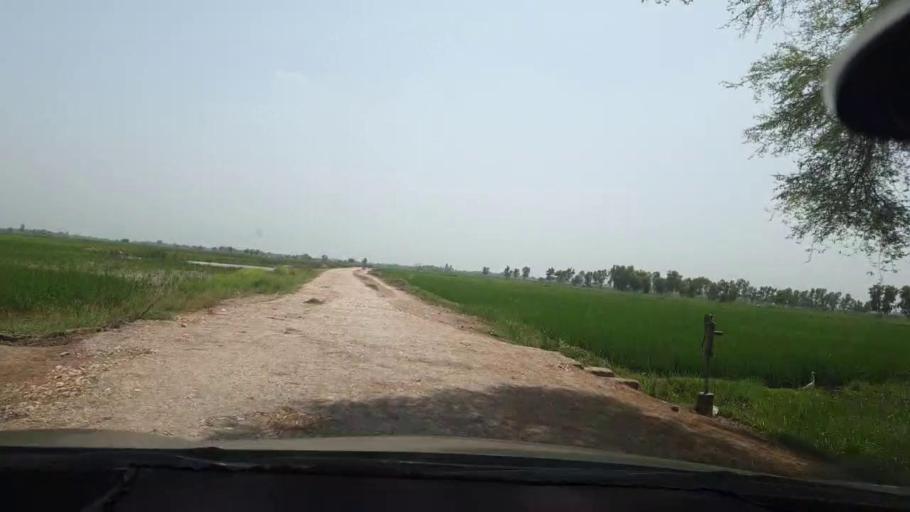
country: PK
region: Sindh
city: Kambar
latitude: 27.6533
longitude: 67.9313
